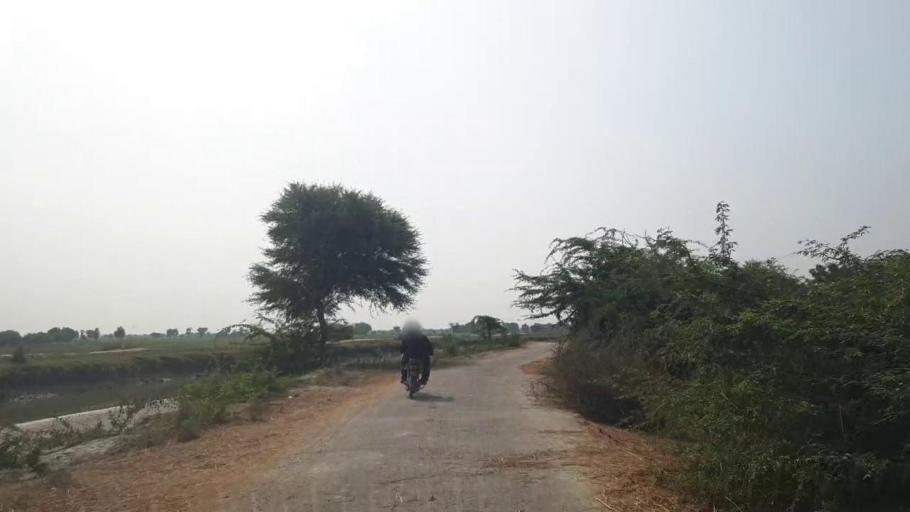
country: PK
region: Sindh
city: Talhar
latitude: 24.7757
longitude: 68.7746
